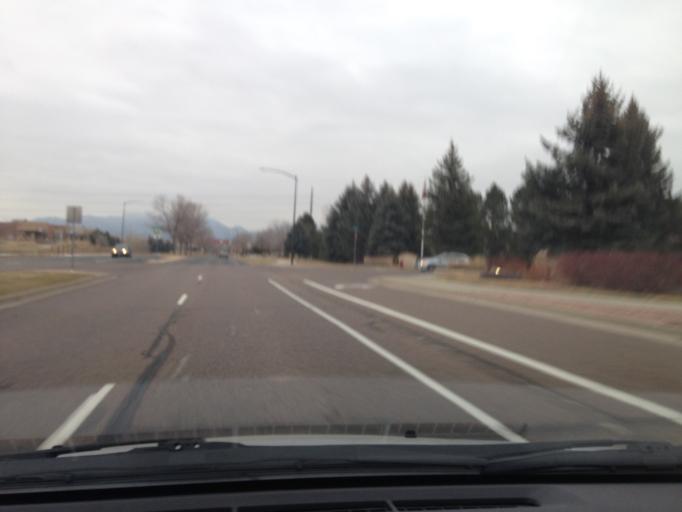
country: US
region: Colorado
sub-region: Boulder County
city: Superior
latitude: 39.9582
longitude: -105.1537
